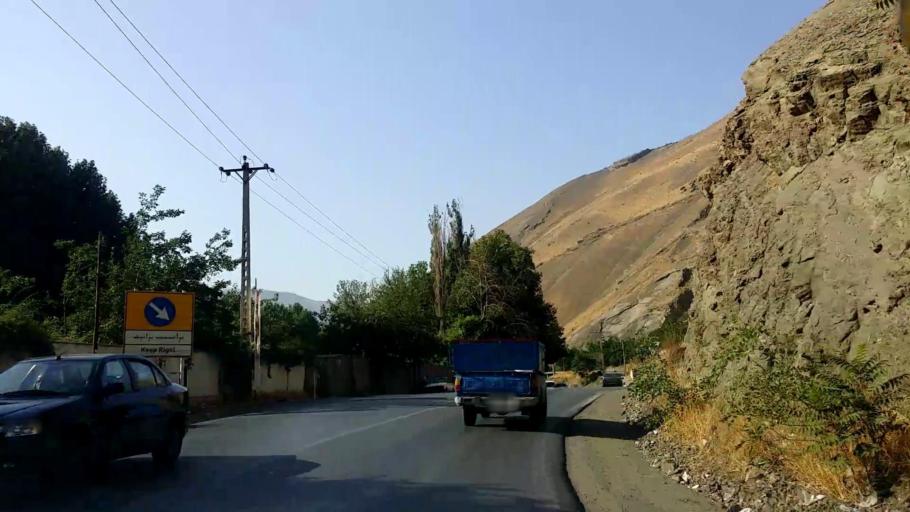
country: IR
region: Alborz
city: Karaj
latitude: 35.8668
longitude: 51.0528
